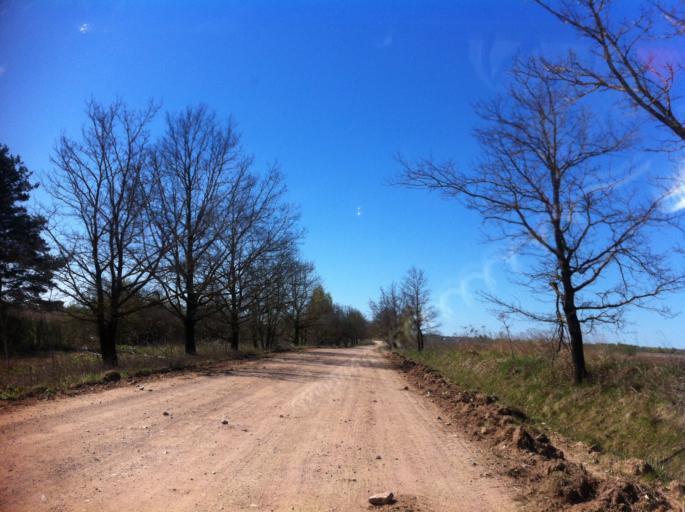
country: RU
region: Pskov
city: Izborsk
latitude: 57.7996
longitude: 27.9672
